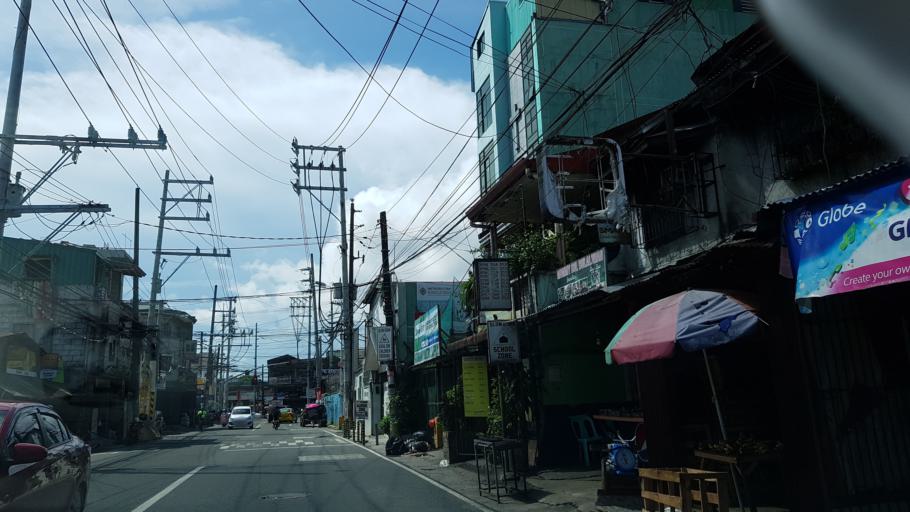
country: PH
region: Metro Manila
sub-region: City of Manila
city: Quiapo
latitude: 14.5795
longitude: 121.0081
